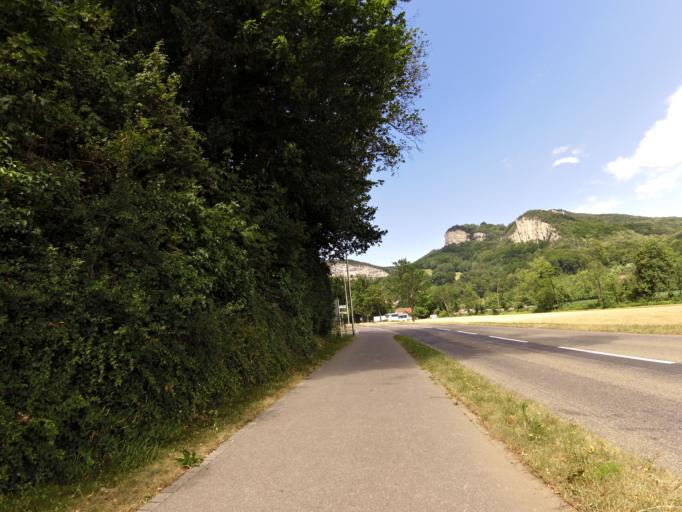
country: CH
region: Solothurn
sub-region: Bezirk Gaeu
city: Oensingen
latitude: 47.2908
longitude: 7.7041
